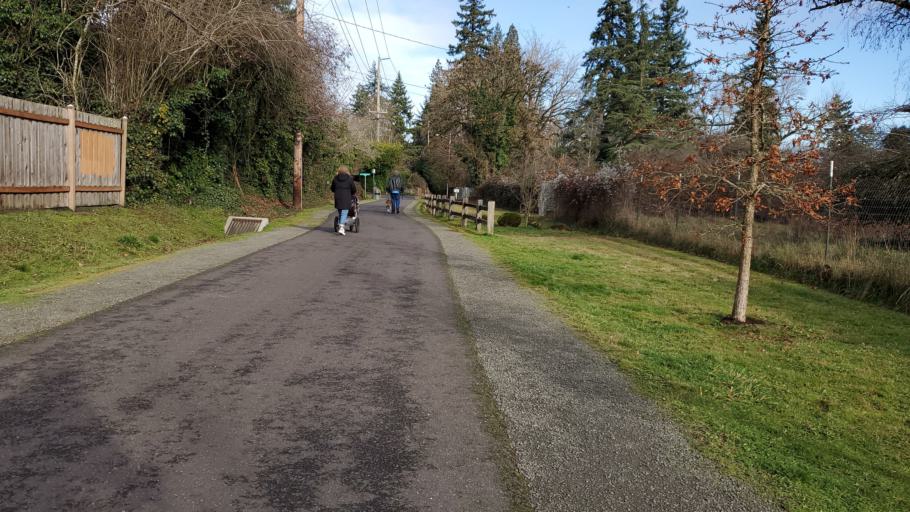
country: US
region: Oregon
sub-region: Clackamas County
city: Oak Grove
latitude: 45.4268
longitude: -122.6390
